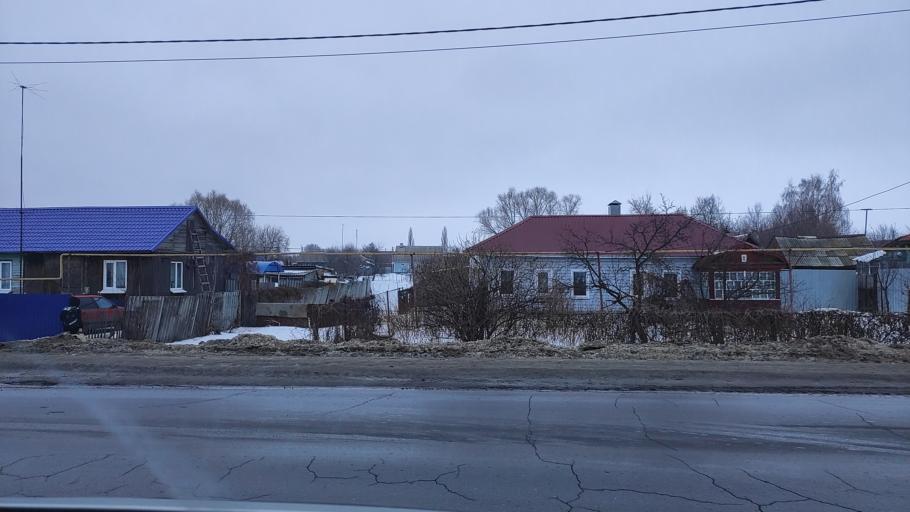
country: RU
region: Tambov
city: Novopokrovka
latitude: 51.9915
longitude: 41.1585
